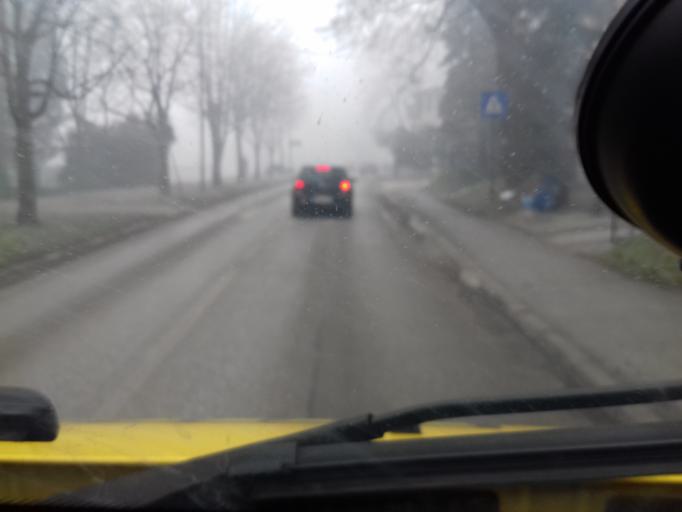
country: BA
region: Federation of Bosnia and Herzegovina
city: Visoko
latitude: 43.9946
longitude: 18.1734
